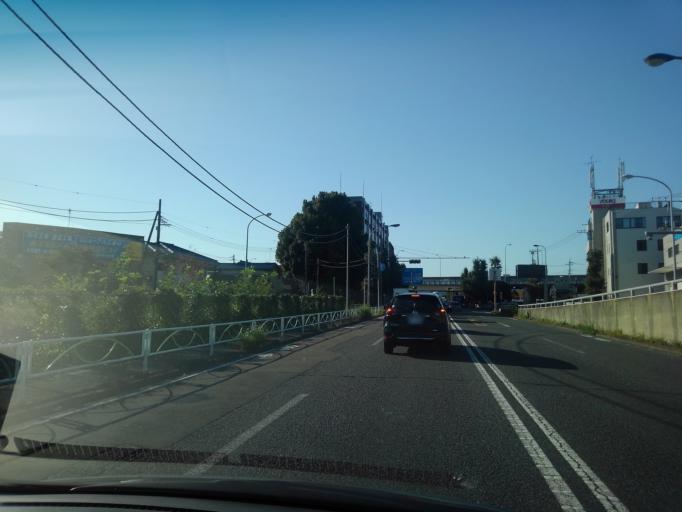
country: JP
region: Tokyo
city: Chofugaoka
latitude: 35.6592
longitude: 139.5340
